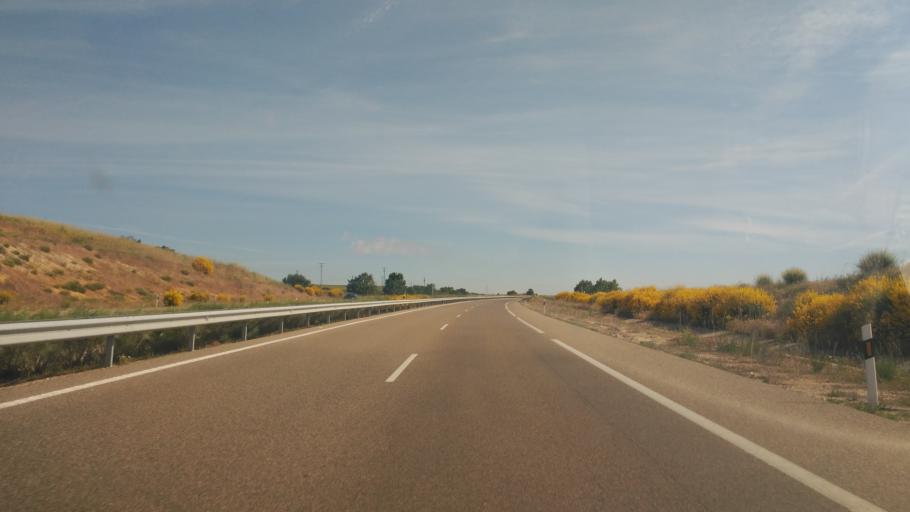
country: ES
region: Castille and Leon
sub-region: Provincia de Zamora
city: Corrales
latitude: 41.3782
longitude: -5.7195
